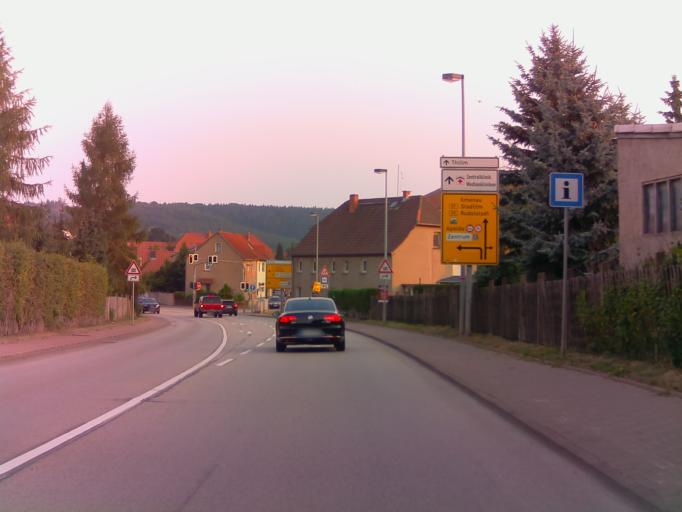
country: DE
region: Thuringia
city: Bad Berka
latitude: 50.9013
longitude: 11.2806
